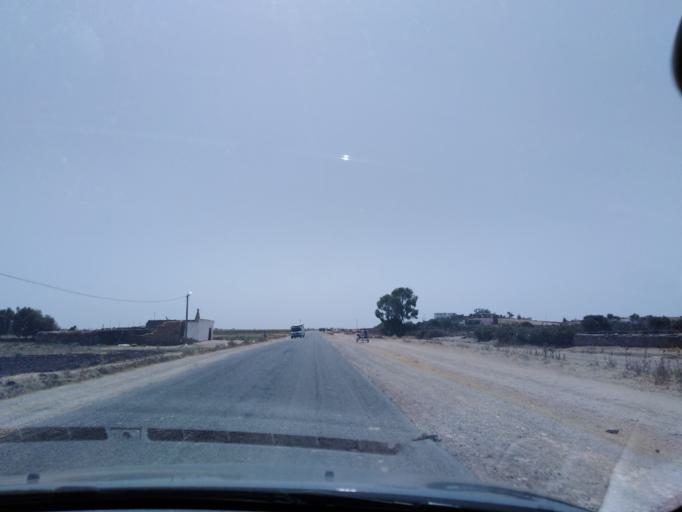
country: MA
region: Doukkala-Abda
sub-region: Safi
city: Safi
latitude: 32.4767
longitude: -8.8751
